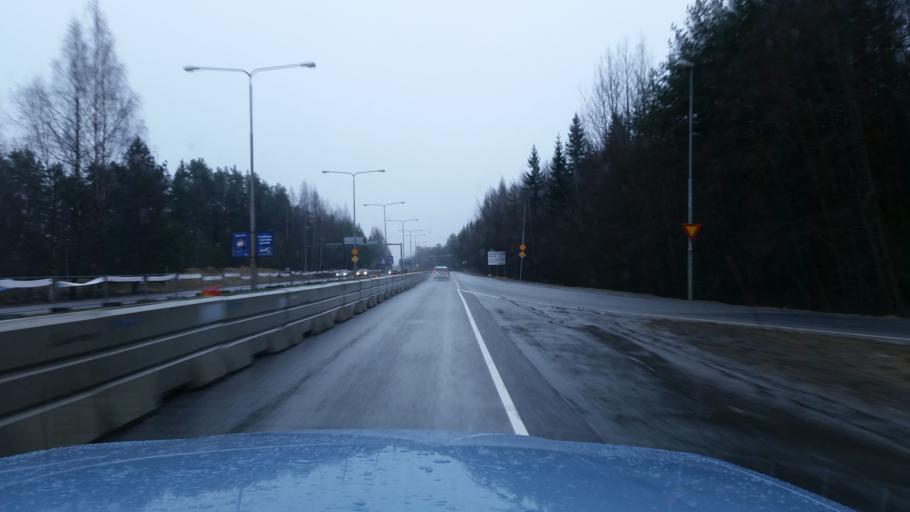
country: FI
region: Pirkanmaa
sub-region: Tampere
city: Tampere
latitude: 61.4682
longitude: 23.8411
